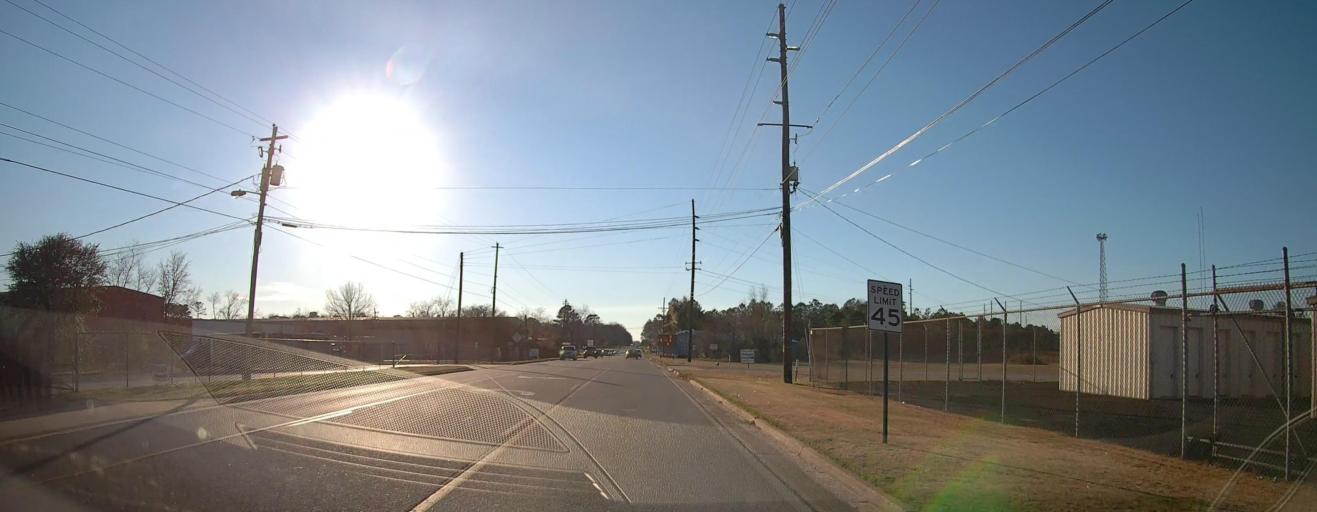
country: US
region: Georgia
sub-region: Dougherty County
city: Albany
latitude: 31.6227
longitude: -84.1893
